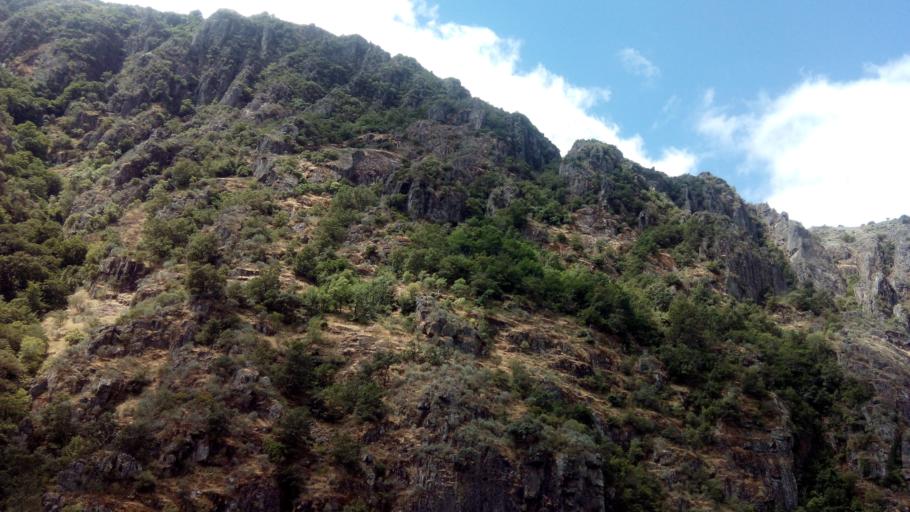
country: ES
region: Galicia
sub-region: Provincia de Lugo
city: Sober
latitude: 42.3848
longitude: -7.6178
